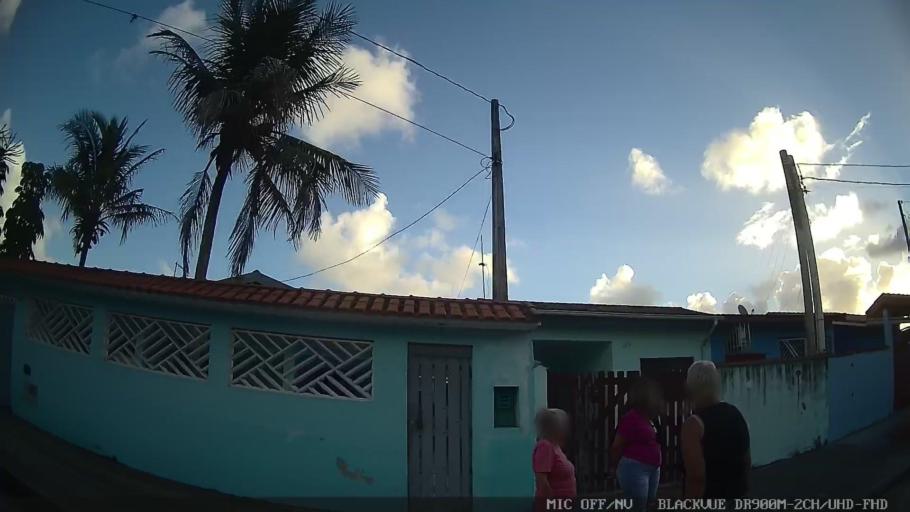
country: BR
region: Sao Paulo
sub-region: Itanhaem
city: Itanhaem
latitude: -24.1436
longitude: -46.7216
